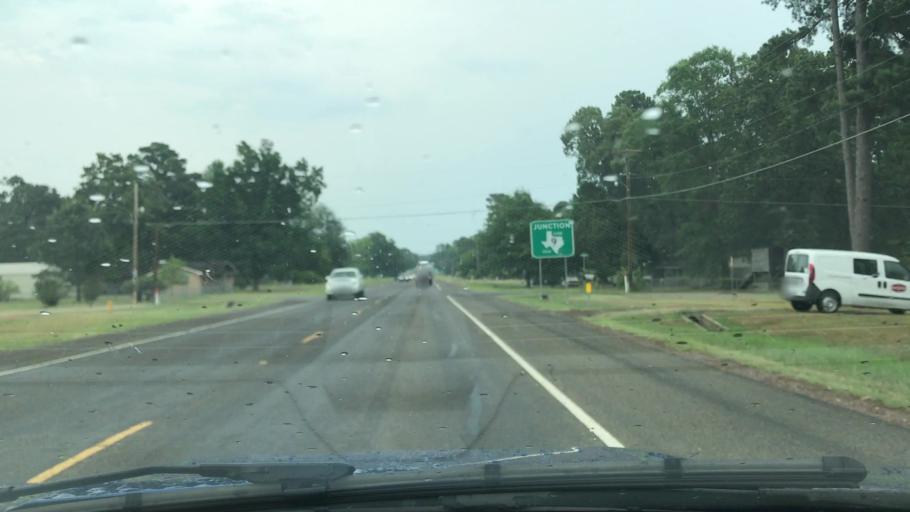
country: US
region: Texas
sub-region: Harrison County
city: Waskom
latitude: 32.4792
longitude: -94.0742
